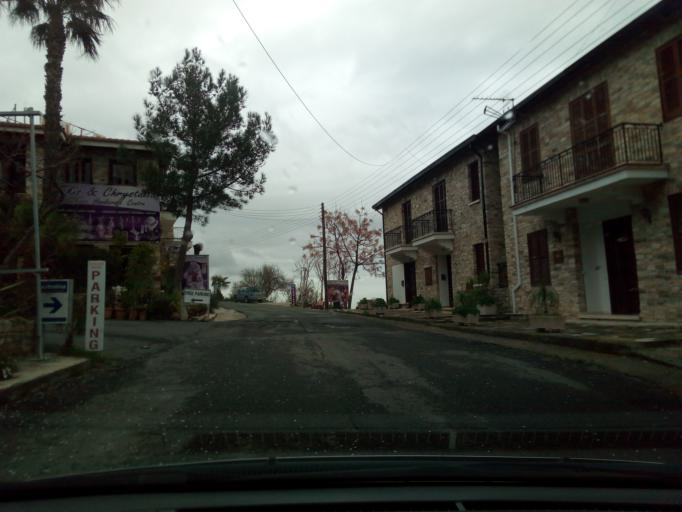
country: CY
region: Lefkosia
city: Lythrodontas
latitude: 34.8626
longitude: 33.3069
